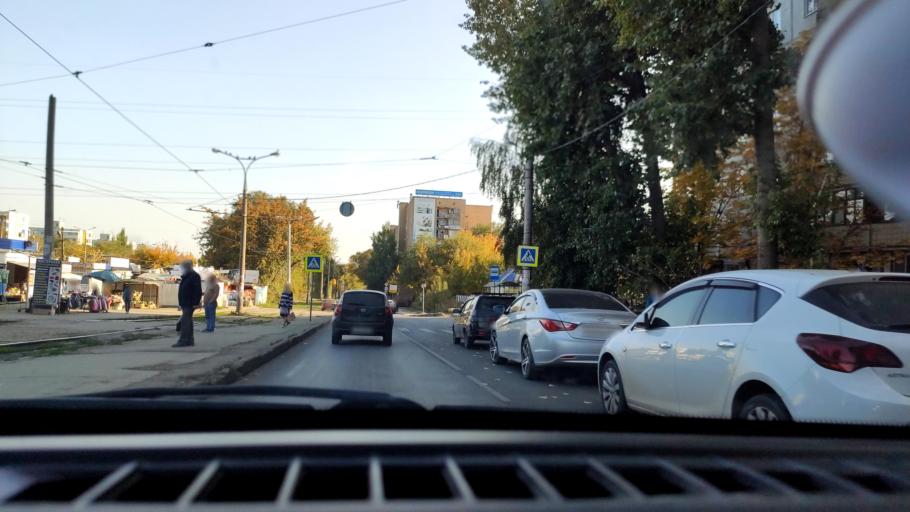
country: RU
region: Samara
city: Samara
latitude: 53.2446
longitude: 50.2515
